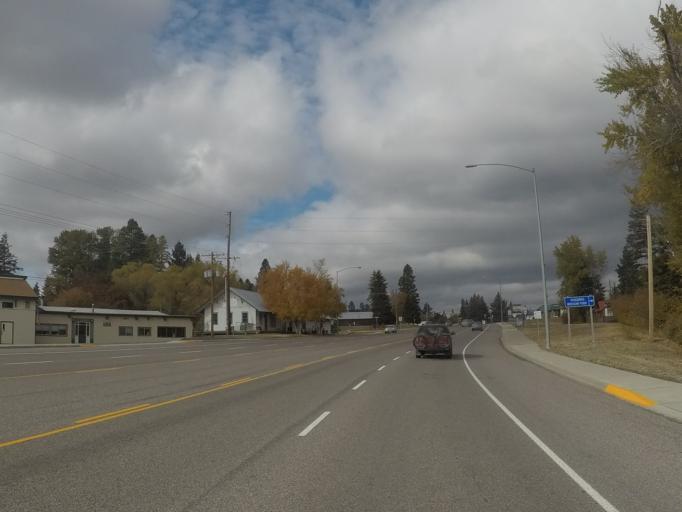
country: US
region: Montana
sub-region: Flathead County
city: Columbia Falls
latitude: 48.3680
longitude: -114.1782
